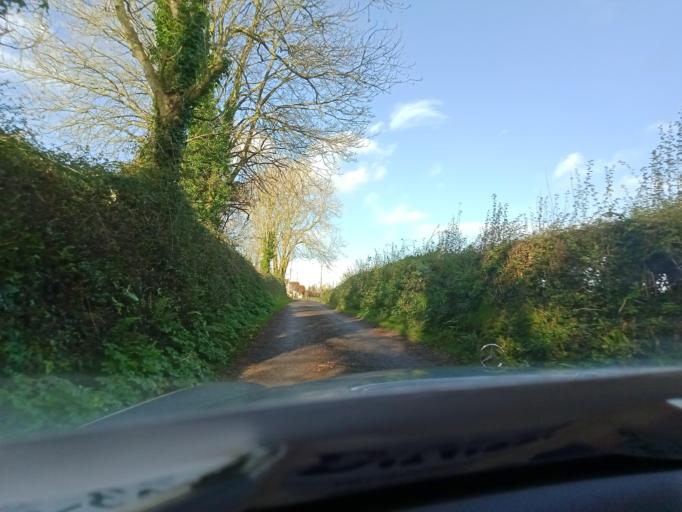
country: IE
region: Munster
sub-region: Waterford
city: Portlaw
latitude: 52.3070
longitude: -7.2865
